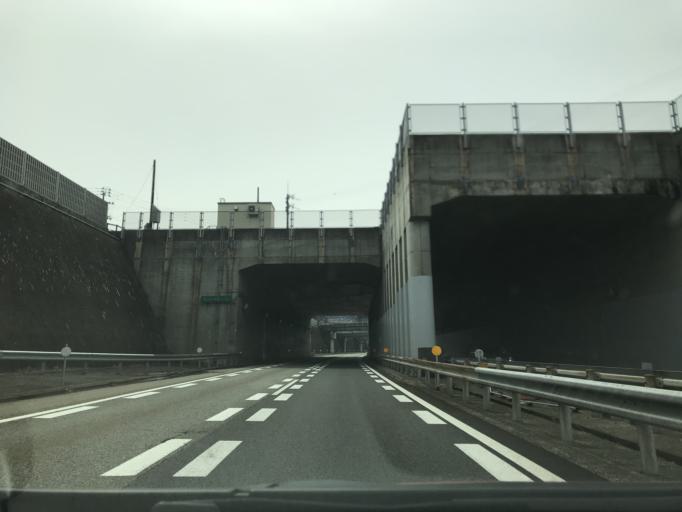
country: JP
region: Niigata
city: Ojiya
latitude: 37.2342
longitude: 138.9751
